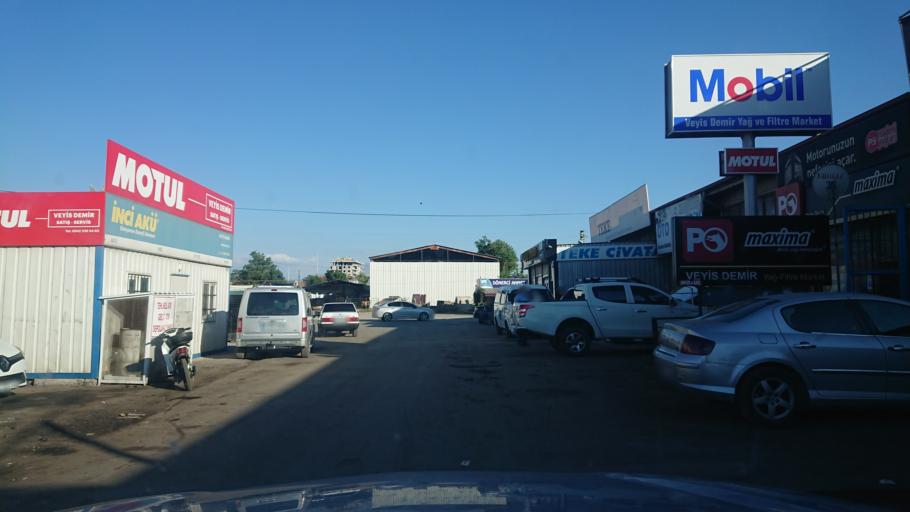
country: TR
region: Aksaray
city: Aksaray
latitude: 38.3727
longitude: 33.9935
